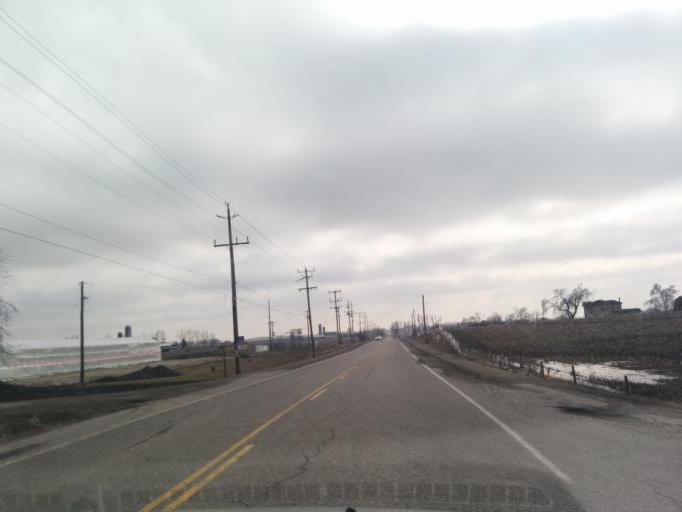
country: CA
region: Ontario
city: Waterloo
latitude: 43.6329
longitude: -80.5500
